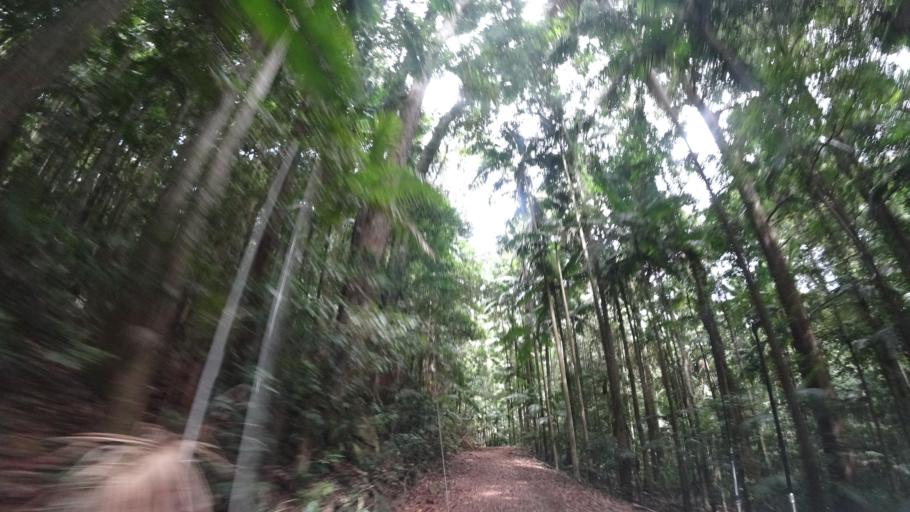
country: AU
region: Queensland
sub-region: Moreton Bay
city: Highvale
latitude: -27.3323
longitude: 152.7618
